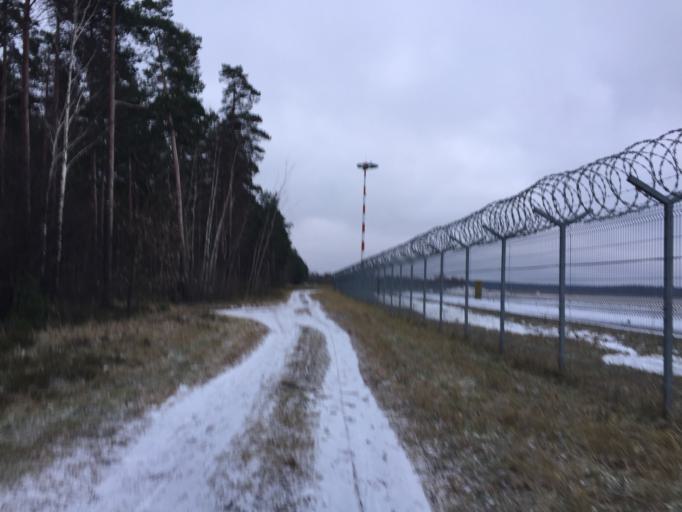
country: LV
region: Babite
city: Pinki
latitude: 56.9087
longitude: 23.9742
